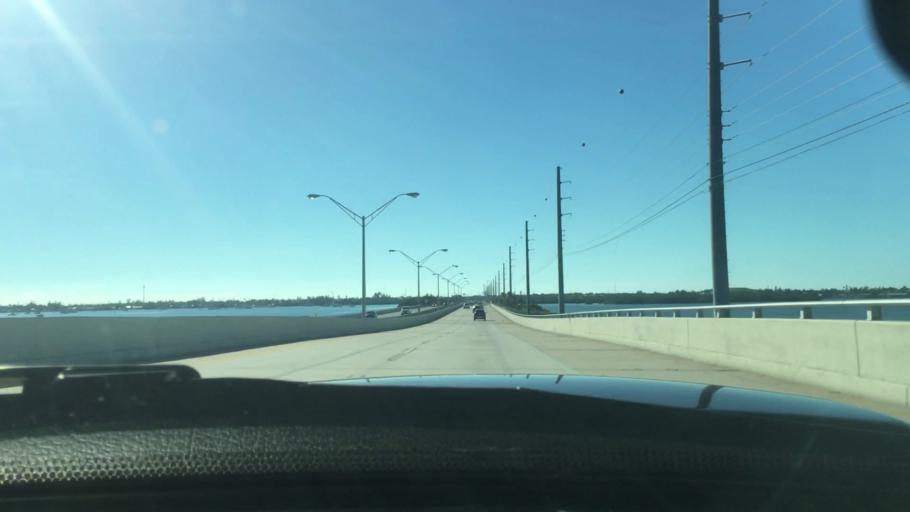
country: US
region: Florida
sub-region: Monroe County
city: Stock Island
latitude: 24.5777
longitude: -81.7169
